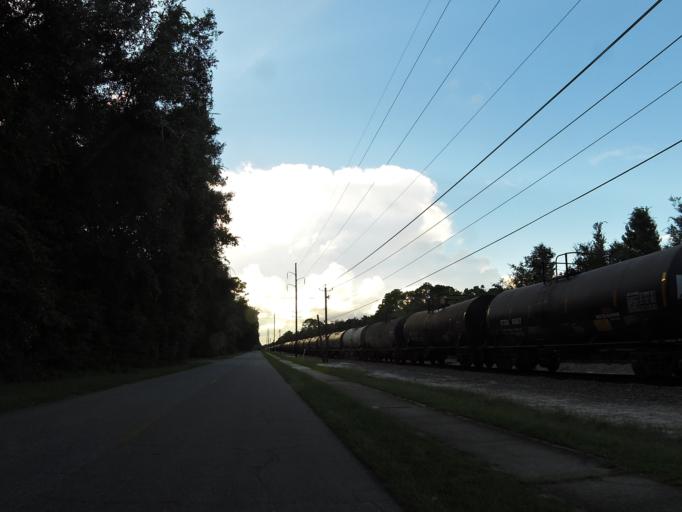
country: US
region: Georgia
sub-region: Camden County
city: St Marys
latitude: 30.7431
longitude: -81.5679
